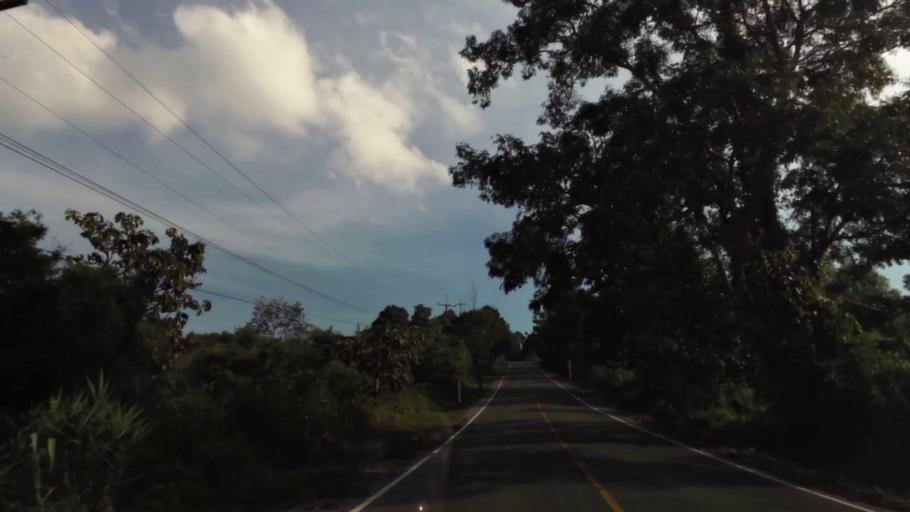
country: TH
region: Chiang Rai
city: Khun Tan
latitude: 19.8740
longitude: 100.3206
